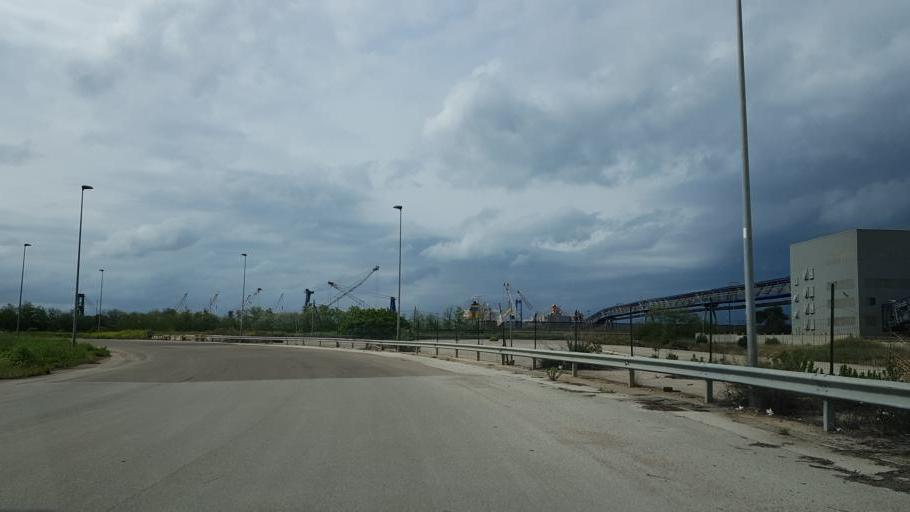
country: IT
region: Apulia
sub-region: Provincia di Brindisi
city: Materdomini
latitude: 40.6421
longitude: 17.9731
